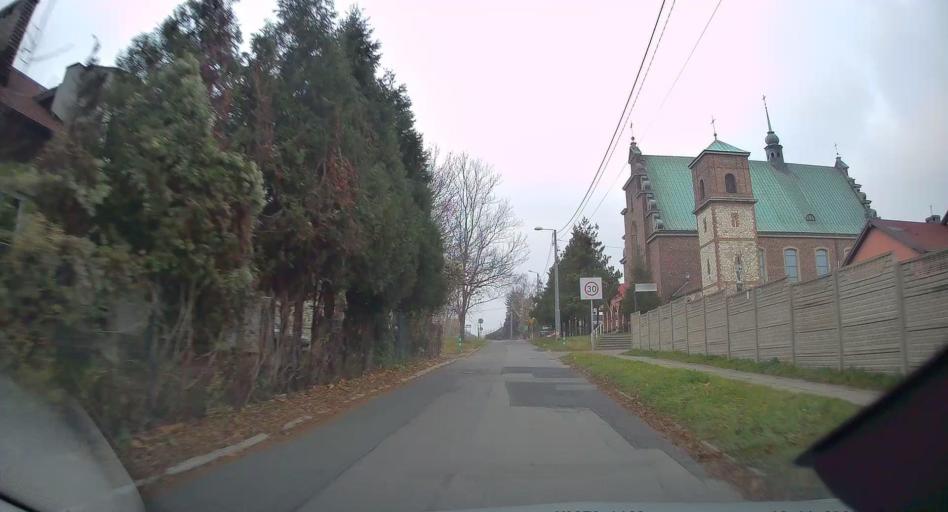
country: PL
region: Silesian Voivodeship
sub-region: Czestochowa
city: Czestochowa
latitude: 50.8175
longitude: 19.0941
